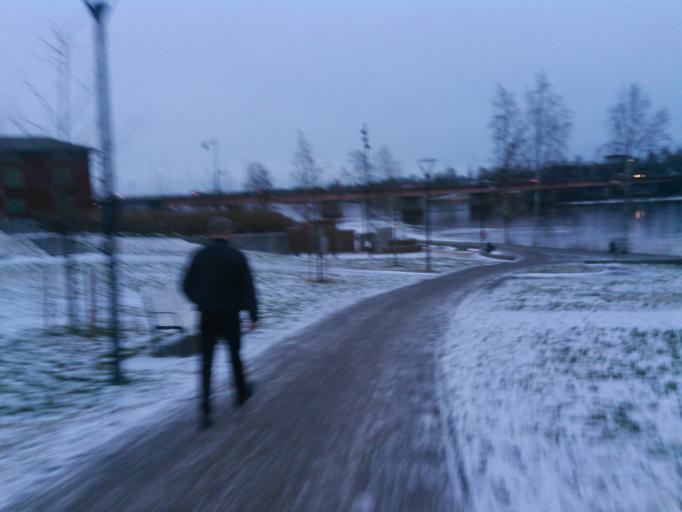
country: SE
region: Vaesterbotten
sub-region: Umea Kommun
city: Umea
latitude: 63.8262
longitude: 20.2519
